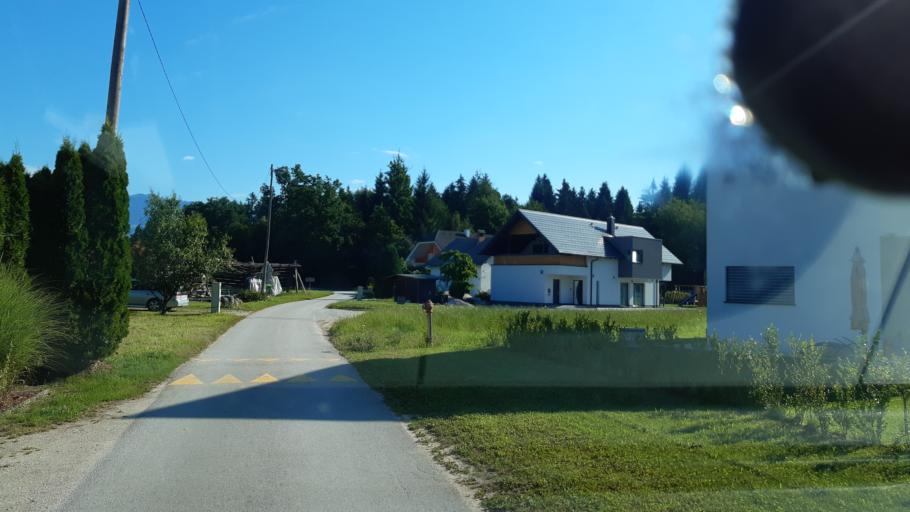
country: SI
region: Vodice
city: Vodice
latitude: 46.1795
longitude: 14.5068
